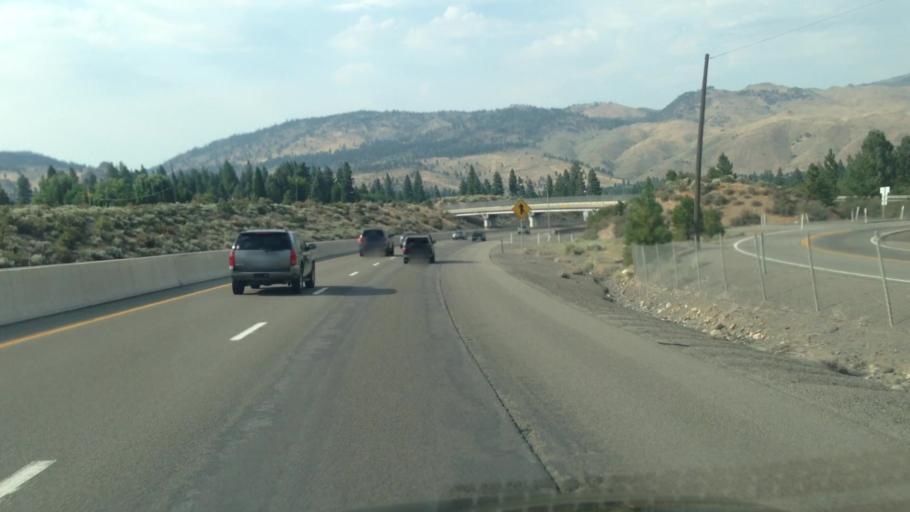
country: US
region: Nevada
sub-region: Washoe County
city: Verdi
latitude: 39.5044
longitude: -119.9992
